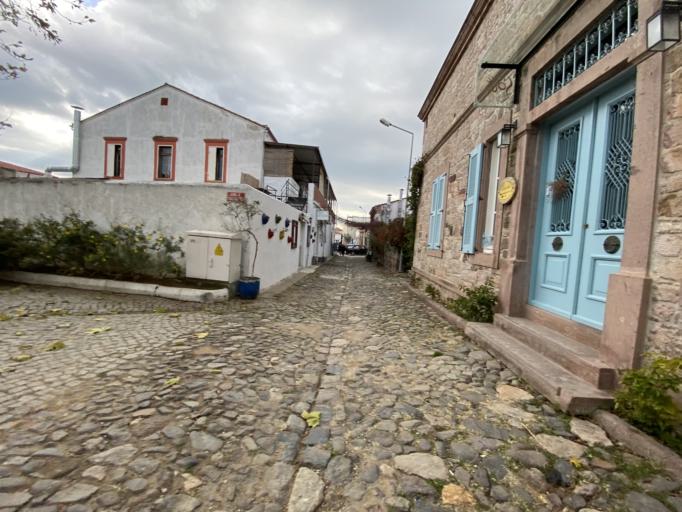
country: TR
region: Balikesir
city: Ayvalik
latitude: 39.3329
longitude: 26.6586
